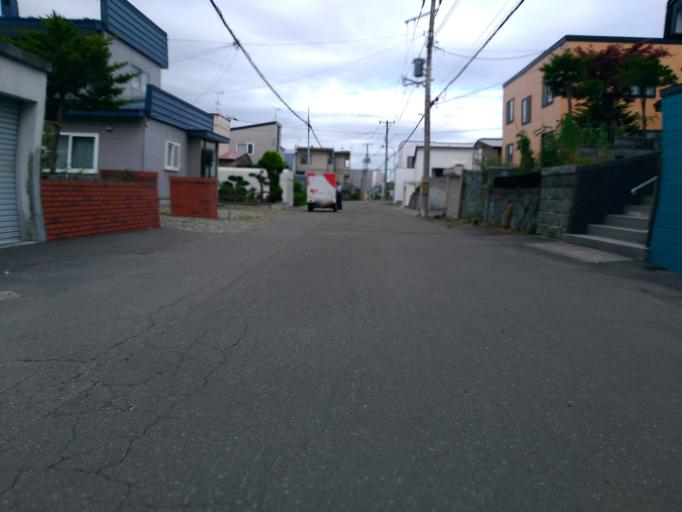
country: JP
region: Hokkaido
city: Ebetsu
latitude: 43.0835
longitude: 141.5236
